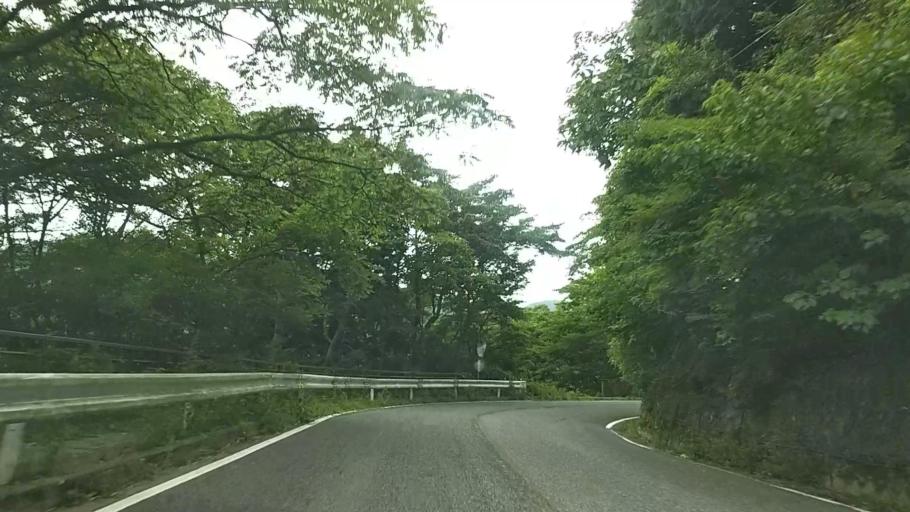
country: JP
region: Kanagawa
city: Hakone
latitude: 35.2080
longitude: 139.0570
